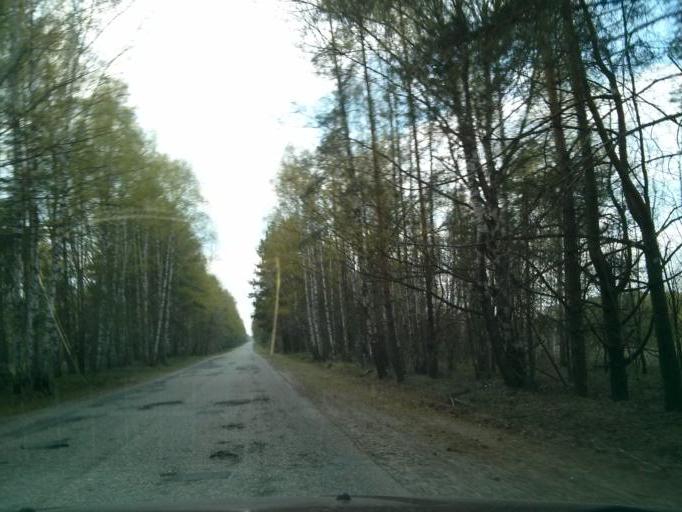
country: RU
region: Nizjnij Novgorod
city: Shimorskoye
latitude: 55.3409
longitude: 41.8514
